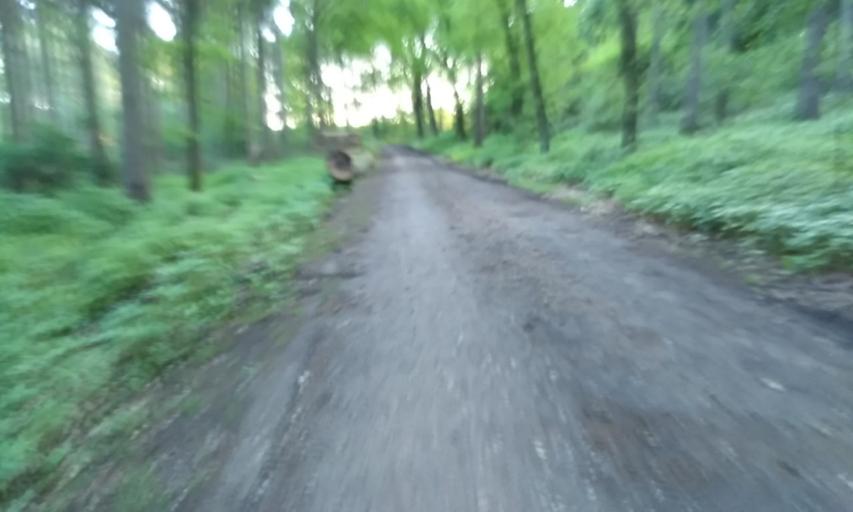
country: DE
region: Lower Saxony
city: Bliedersdorf
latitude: 53.4915
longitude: 9.5421
